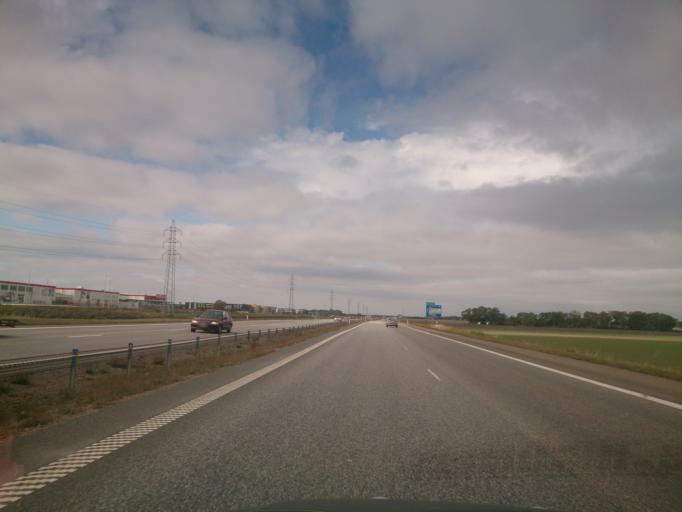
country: SE
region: OEstergoetland
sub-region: Linkopings Kommun
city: Linkoping
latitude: 58.4344
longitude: 15.6149
